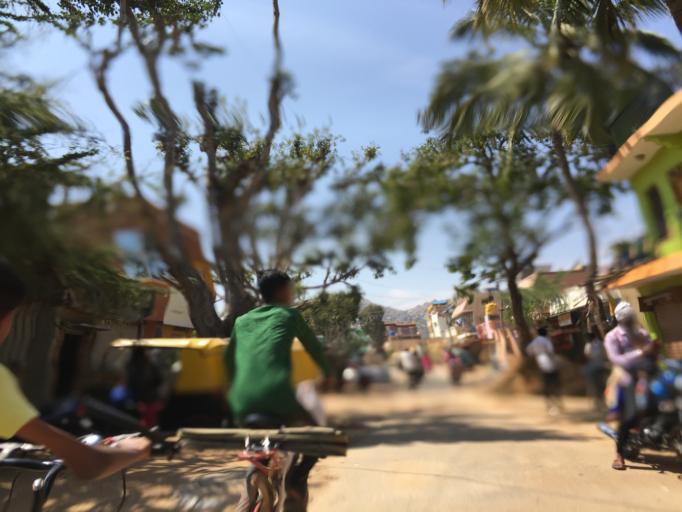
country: IN
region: Karnataka
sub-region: Kolar
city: Kolar
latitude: 13.1380
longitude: 78.1182
